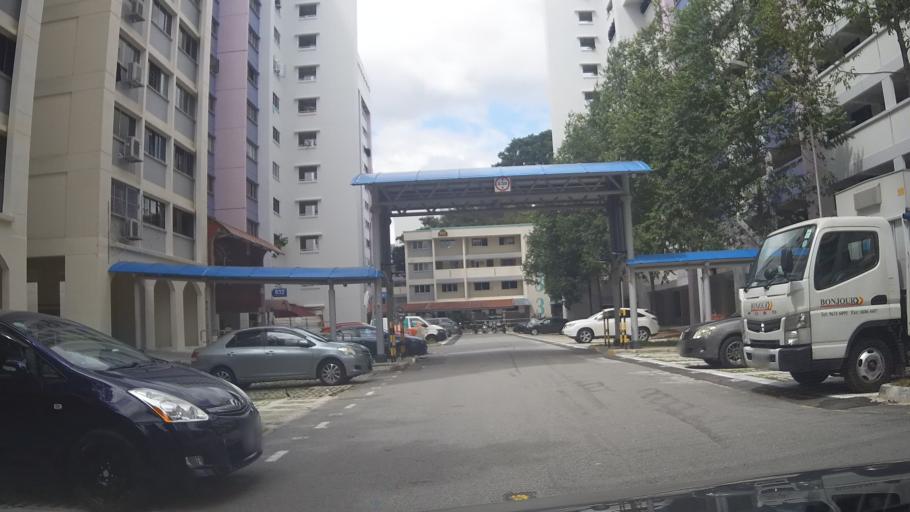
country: MY
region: Johor
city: Johor Bahru
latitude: 1.4400
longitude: 103.7916
